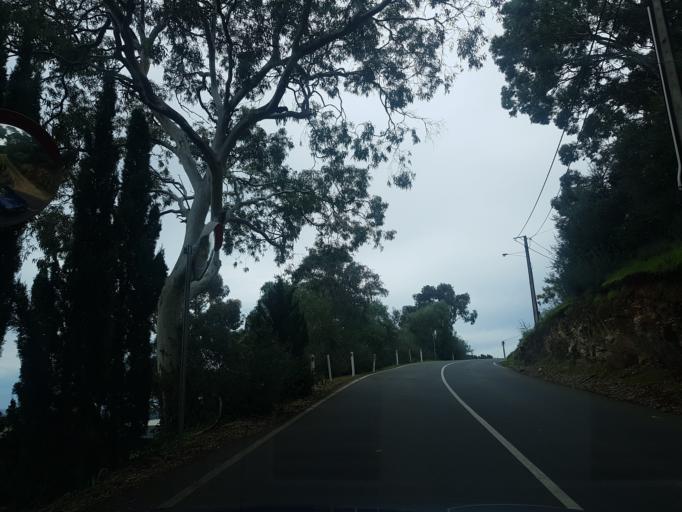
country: AU
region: South Australia
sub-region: Burnside
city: Mount Osmond
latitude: -34.9631
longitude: 138.6505
